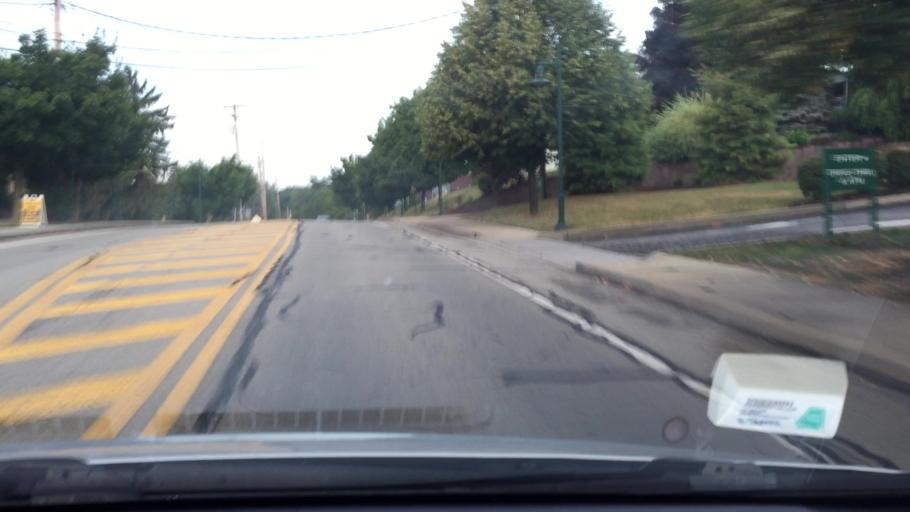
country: US
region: Pennsylvania
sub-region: Allegheny County
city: Bradford Woods
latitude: 40.6260
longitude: -80.0567
